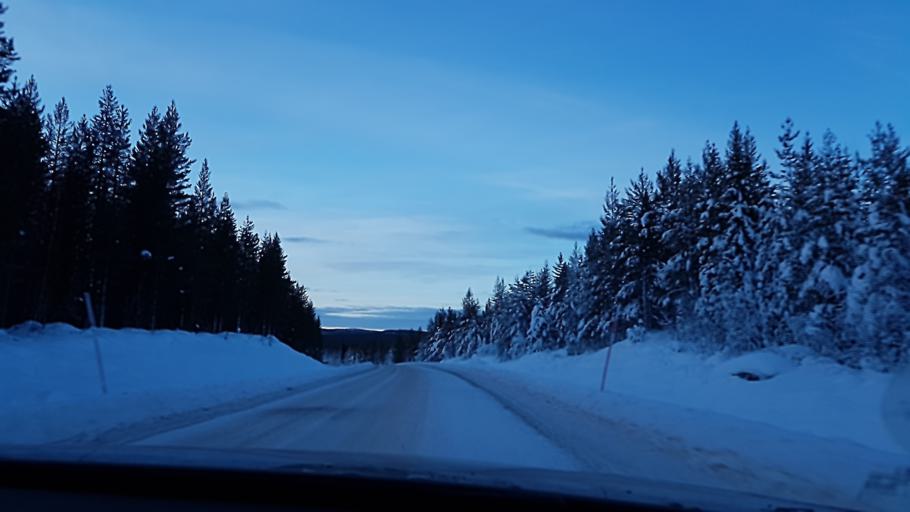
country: SE
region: Norrbotten
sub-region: Arvidsjaurs Kommun
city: Arvidsjaur
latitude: 65.9596
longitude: 19.5383
